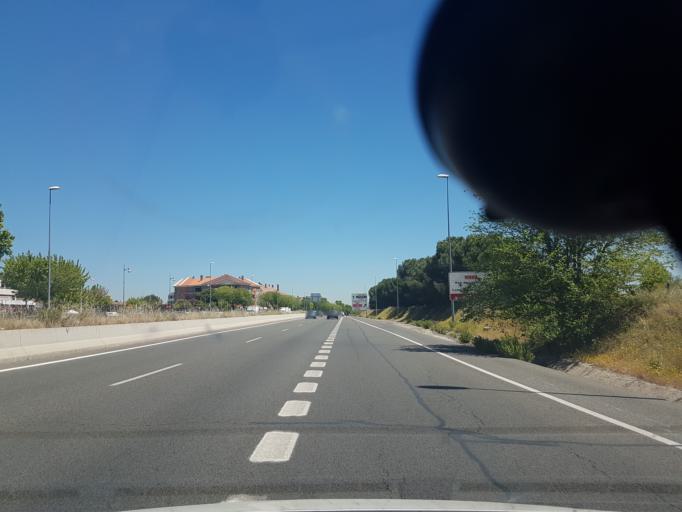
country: ES
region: Madrid
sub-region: Provincia de Madrid
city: Pozuelo de Alarcon
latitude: 40.4360
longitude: -3.7938
